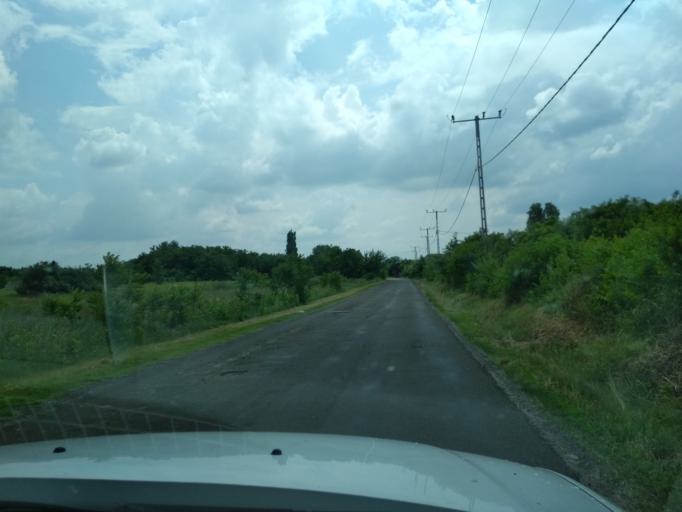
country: HU
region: Pest
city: Tapioszentmarton
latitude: 47.3770
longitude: 19.7568
